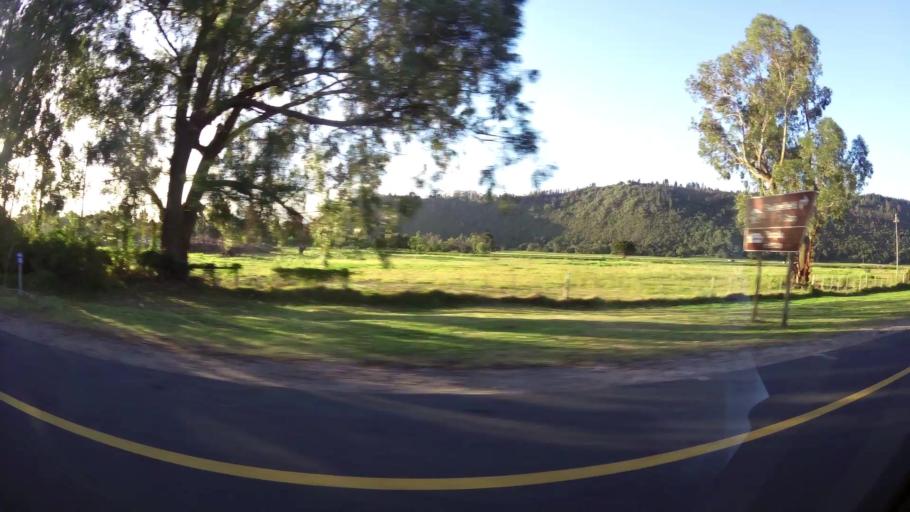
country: ZA
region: Western Cape
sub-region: Eden District Municipality
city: Knysna
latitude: -34.0092
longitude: 22.7786
